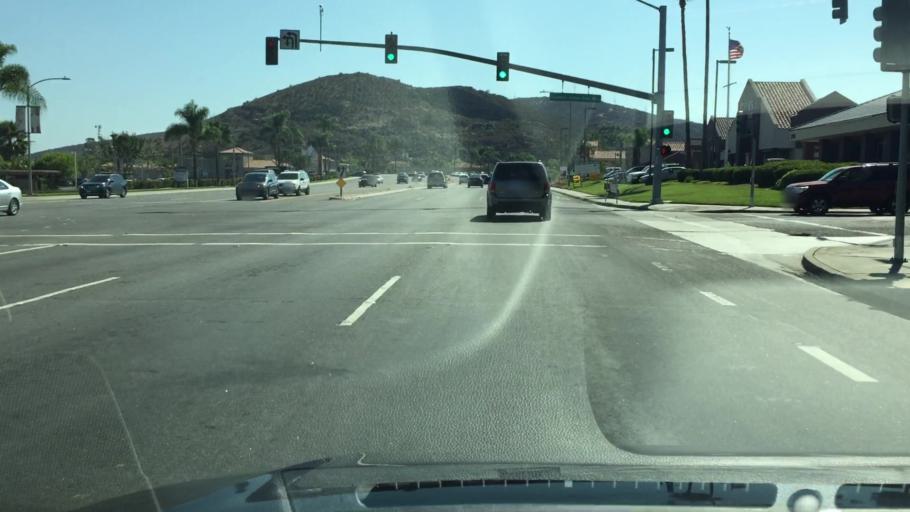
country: US
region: California
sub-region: San Diego County
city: Rancho San Diego
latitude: 32.7411
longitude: -116.9386
